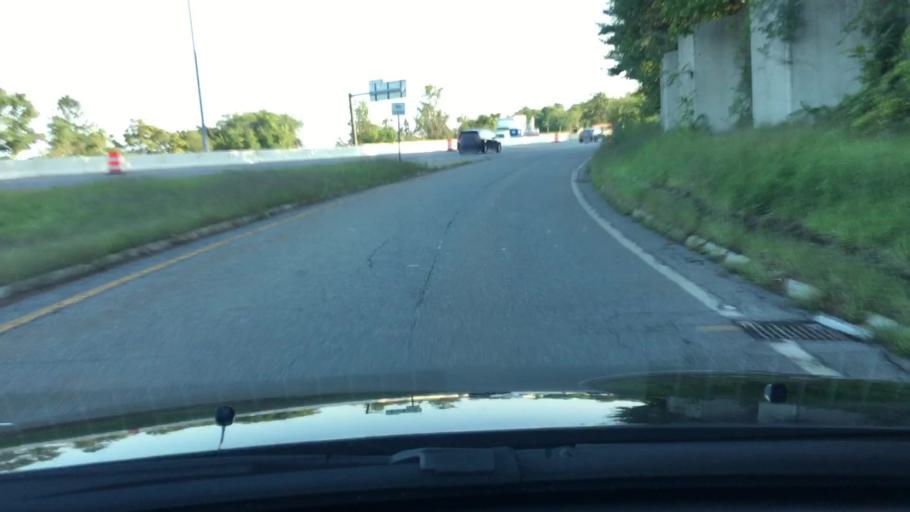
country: US
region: Massachusetts
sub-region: Worcester County
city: West Boylston
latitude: 42.3341
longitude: -71.7988
